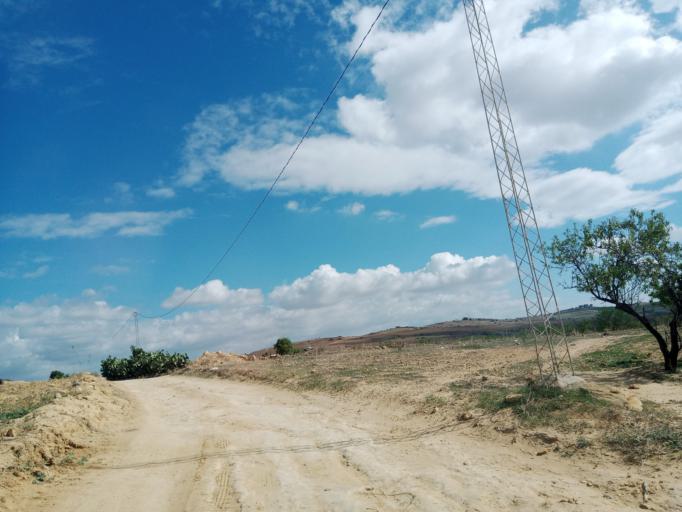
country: TN
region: Tunis
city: Oued Lill
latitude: 36.8084
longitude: 9.9880
